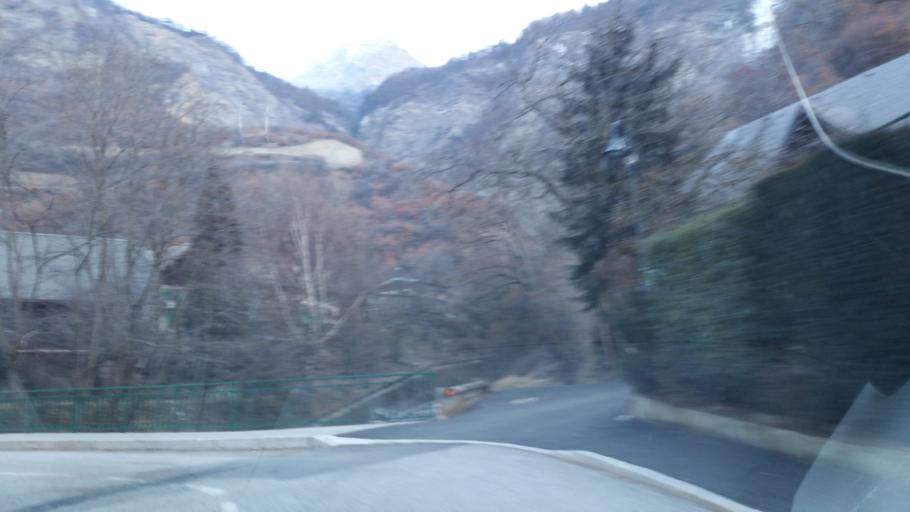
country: FR
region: Rhone-Alpes
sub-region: Departement de la Savoie
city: Saint-Jean-de-Maurienne
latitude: 45.2988
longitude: 6.3649
